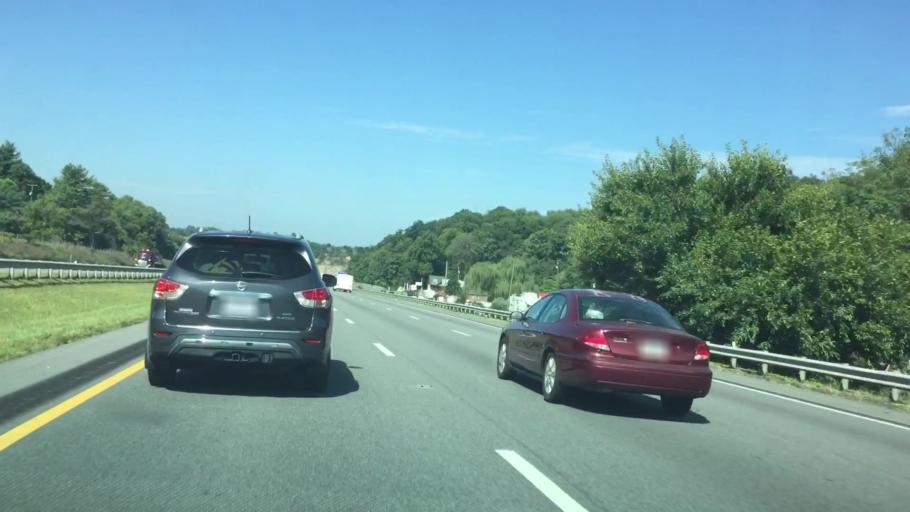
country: US
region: Virginia
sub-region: Wythe County
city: Wytheville
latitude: 36.9414
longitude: -81.0142
